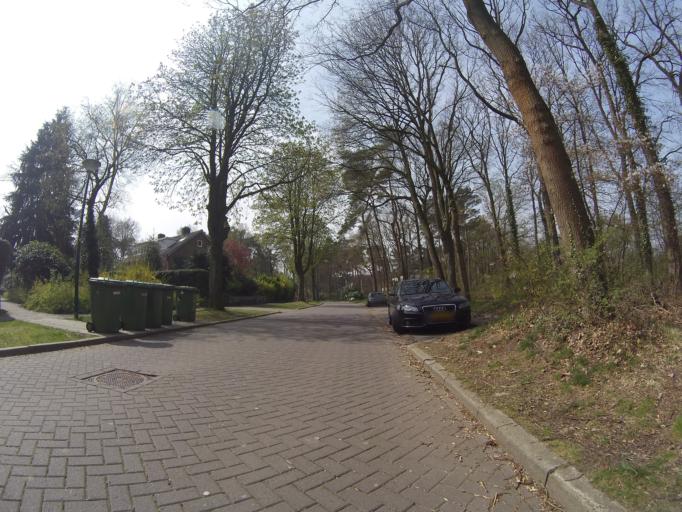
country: NL
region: Utrecht
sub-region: Gemeente Soest
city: Soest
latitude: 52.1619
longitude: 5.2981
